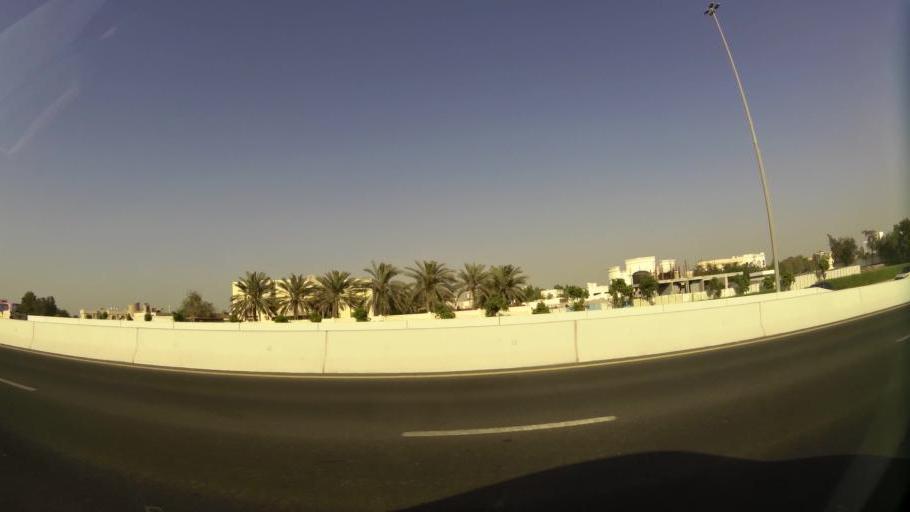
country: AE
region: Ash Shariqah
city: Sharjah
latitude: 25.2506
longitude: 55.3870
